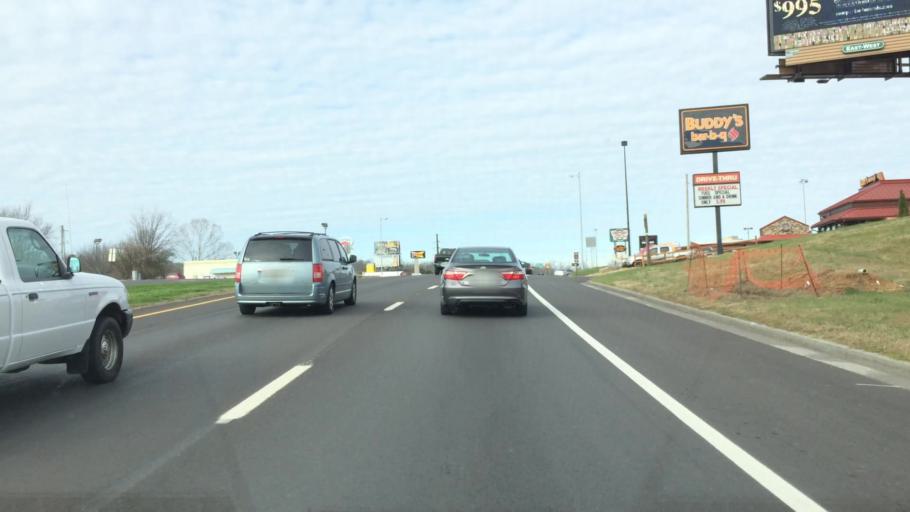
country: US
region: Tennessee
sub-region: McMinn County
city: Athens
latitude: 35.4515
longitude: -84.6246
